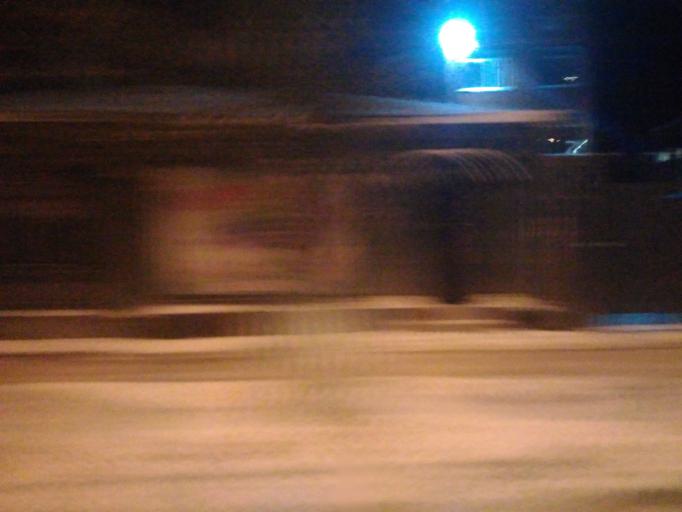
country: RU
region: Ulyanovsk
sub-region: Ulyanovskiy Rayon
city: Ulyanovsk
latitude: 54.3310
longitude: 48.4010
